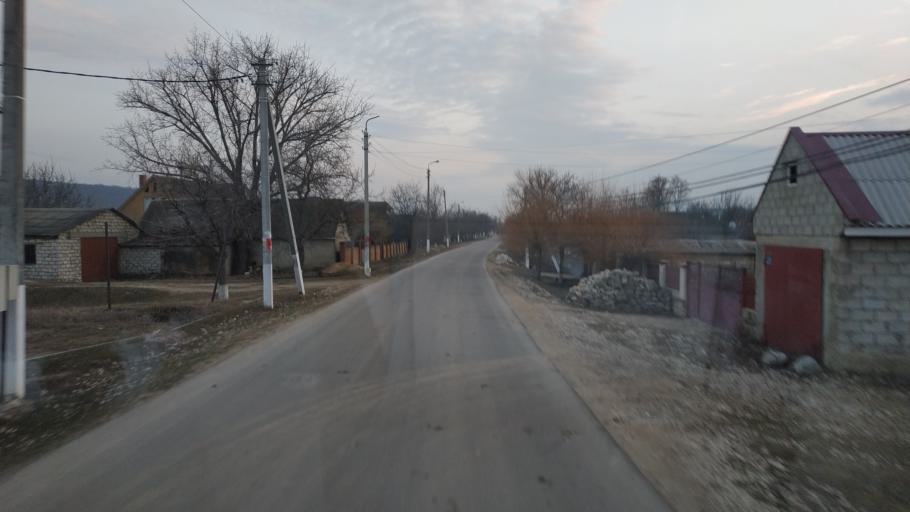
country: RO
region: Vaslui
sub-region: Comuna Stanilesti
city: Stanilesti
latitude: 46.6583
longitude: 28.3062
